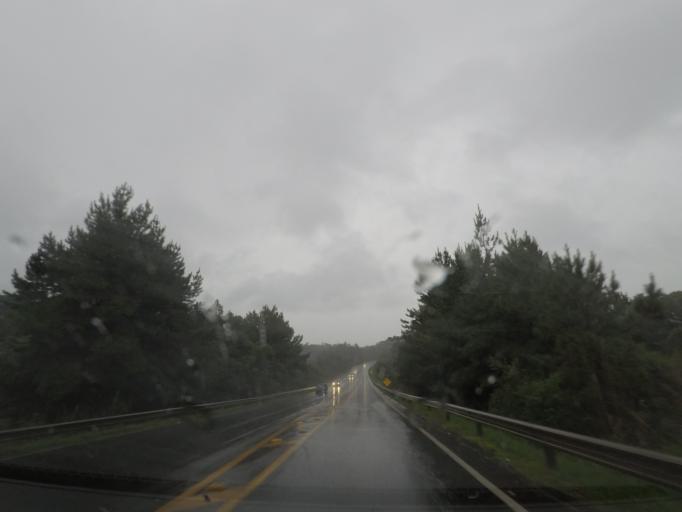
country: BR
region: Parana
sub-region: Almirante Tamandare
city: Almirante Tamandare
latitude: -25.3564
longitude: -49.3093
